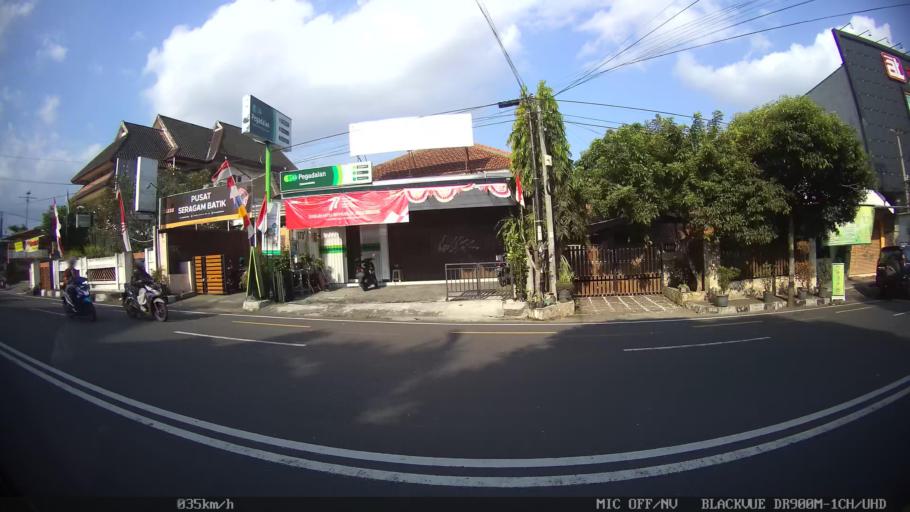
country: ID
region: Daerah Istimewa Yogyakarta
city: Yogyakarta
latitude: -7.7826
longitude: 110.3524
